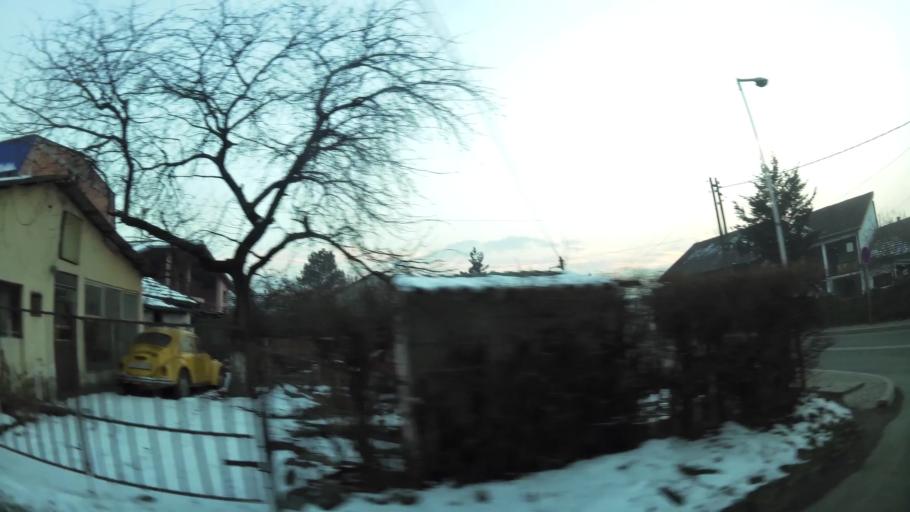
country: MK
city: Creshevo
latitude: 42.0013
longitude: 21.5023
